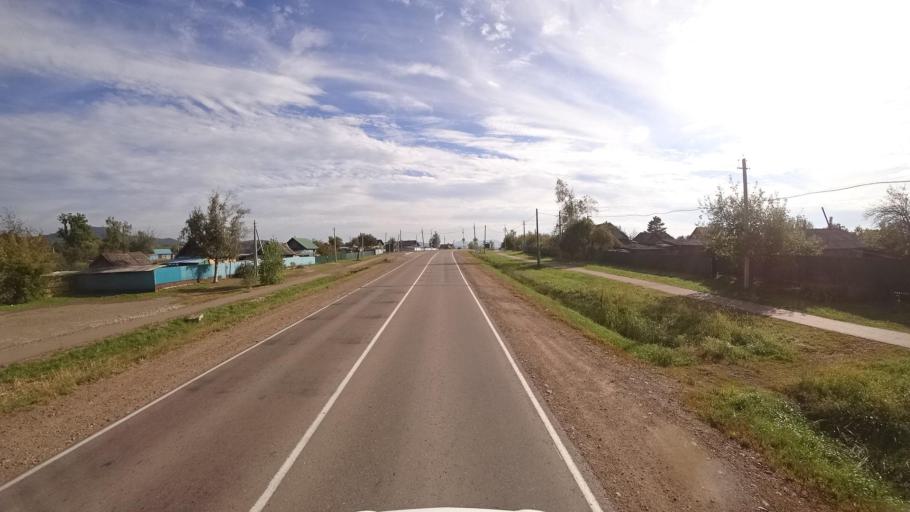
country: RU
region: Primorskiy
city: Dostoyevka
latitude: 44.3027
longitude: 133.4493
